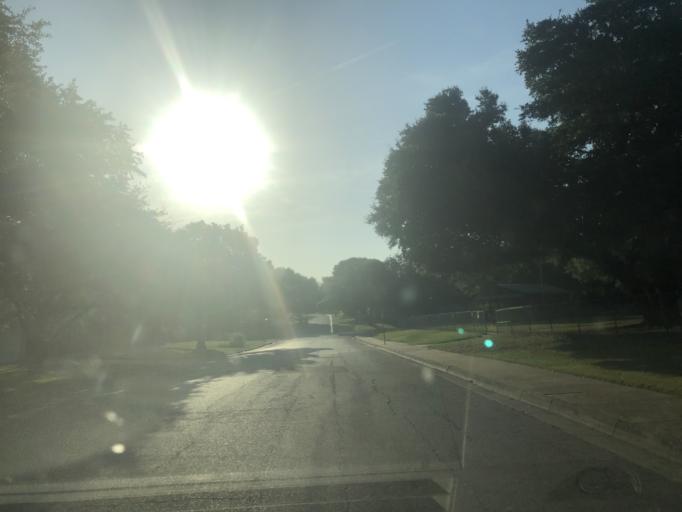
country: US
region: Texas
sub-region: Tarrant County
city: Edgecliff Village
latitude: 32.6549
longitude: -97.3928
